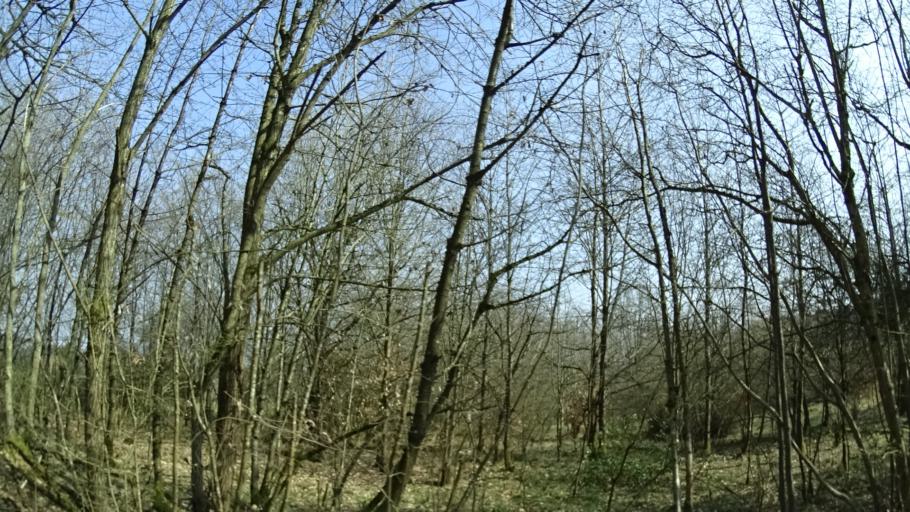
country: DE
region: Rheinland-Pfalz
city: Mettweiler
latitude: 49.5981
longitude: 7.3279
